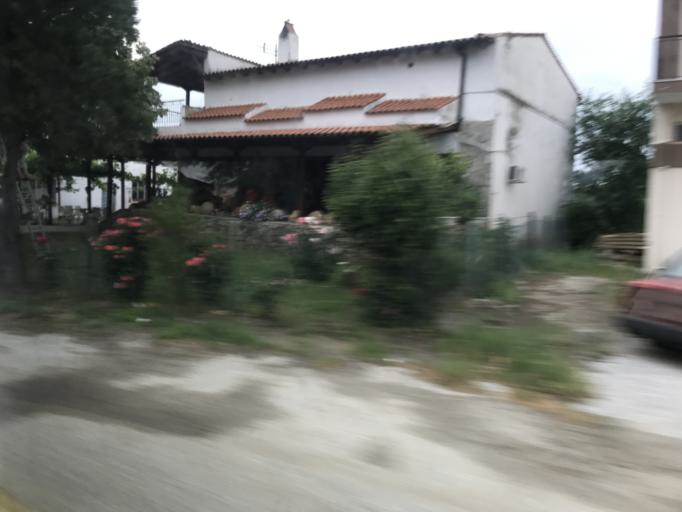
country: GR
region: East Macedonia and Thrace
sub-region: Nomos Rodopis
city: Aratos
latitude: 41.0841
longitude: 25.5390
